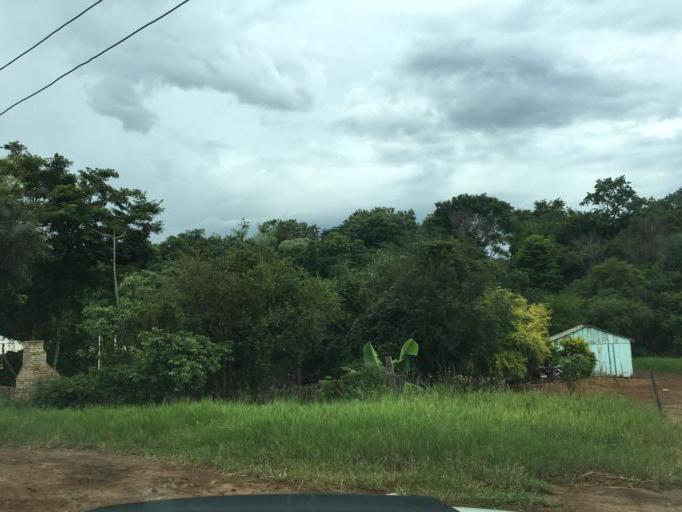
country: PY
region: Alto Parana
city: Ciudad del Este
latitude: -25.4107
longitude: -54.6505
